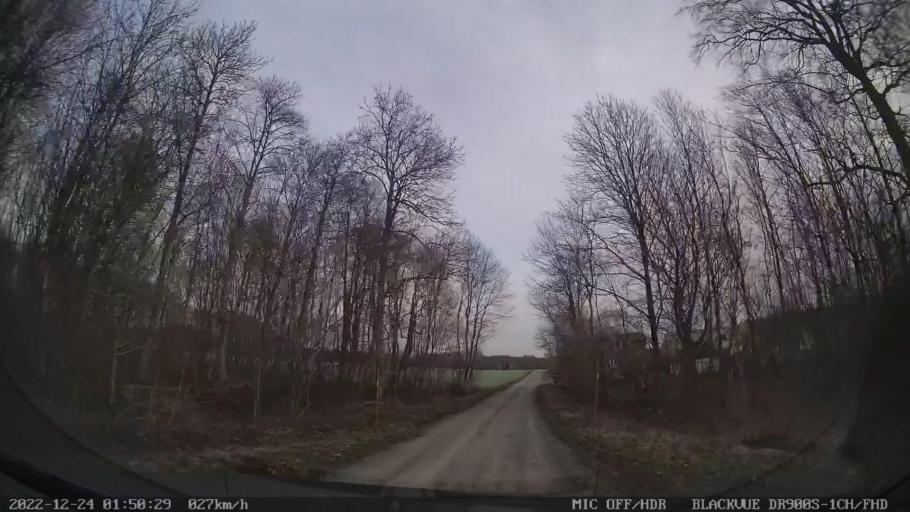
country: SE
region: Skane
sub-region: Simrishamns Kommun
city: Kivik
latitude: 55.5942
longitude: 14.1247
